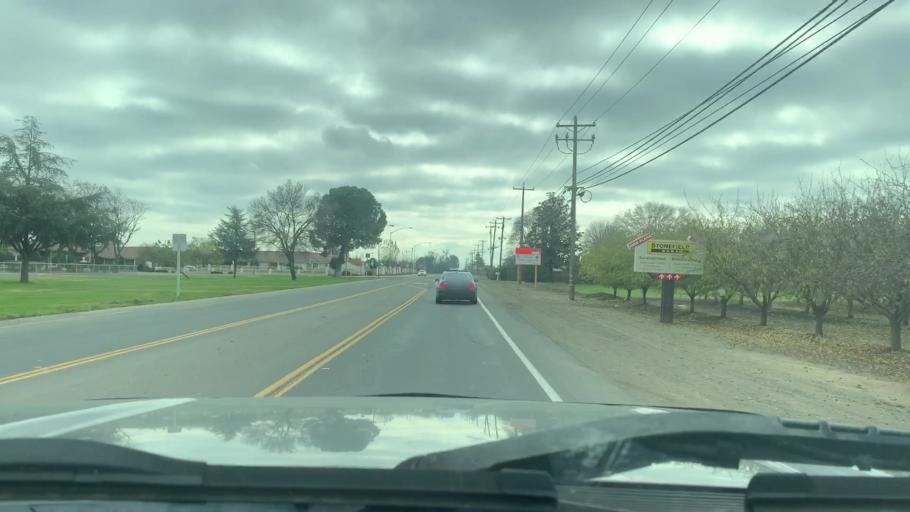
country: US
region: California
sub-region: Merced County
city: Los Banos
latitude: 37.0490
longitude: -120.8356
